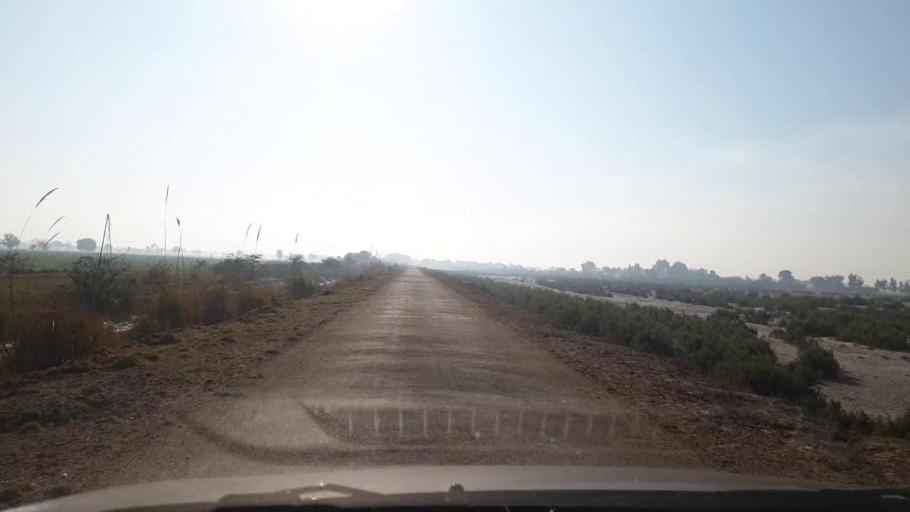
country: PK
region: Sindh
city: Jhol
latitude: 25.9380
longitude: 68.8704
